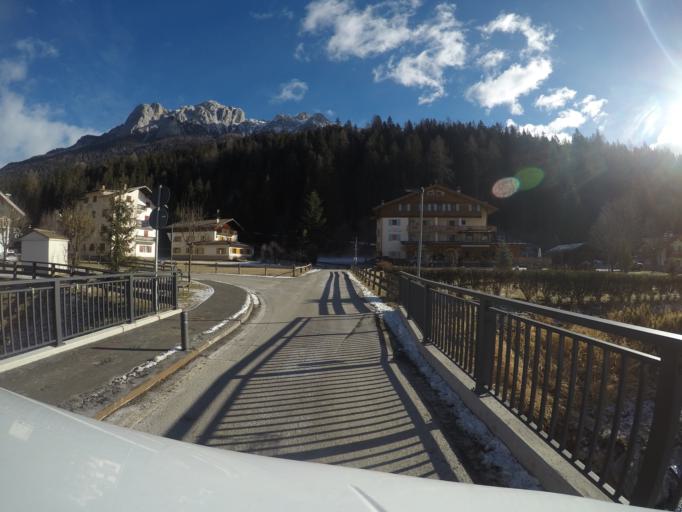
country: IT
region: Trentino-Alto Adige
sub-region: Provincia di Trento
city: Soraga
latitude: 46.3985
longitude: 11.6714
